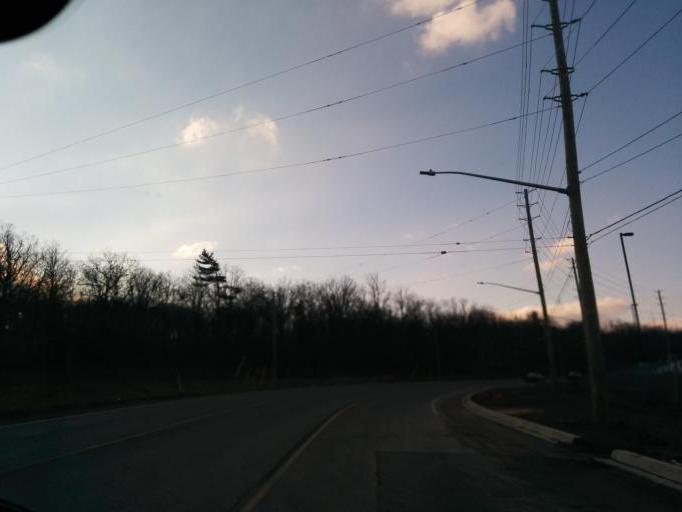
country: CA
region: Ontario
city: Oakville
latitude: 43.4888
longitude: -79.6763
